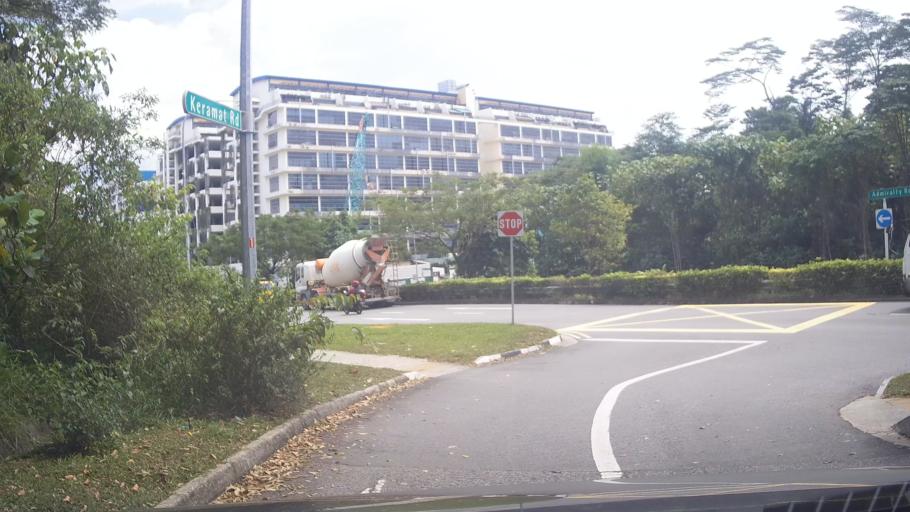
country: MY
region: Johor
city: Johor Bahru
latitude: 1.4521
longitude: 103.7890
